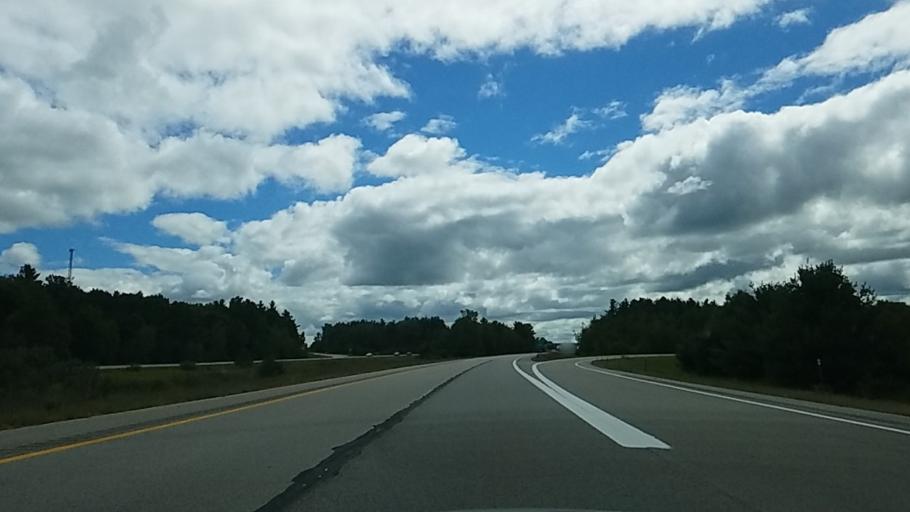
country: US
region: Michigan
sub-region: Arenac County
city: Standish
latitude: 44.0387
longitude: -84.0621
